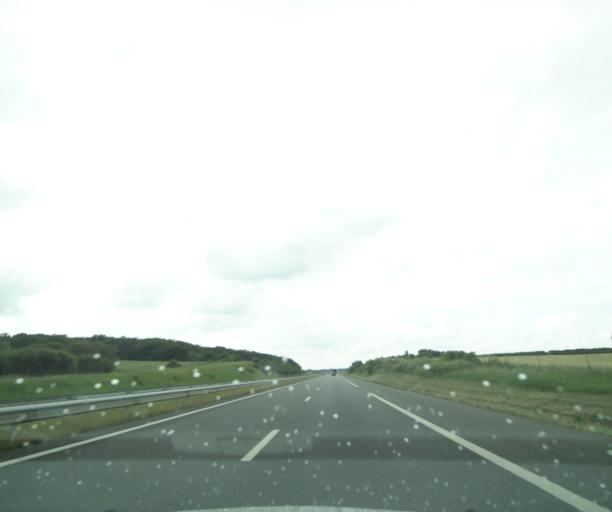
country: FR
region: Centre
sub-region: Departement du Cher
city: Orval
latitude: 46.6722
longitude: 2.4659
